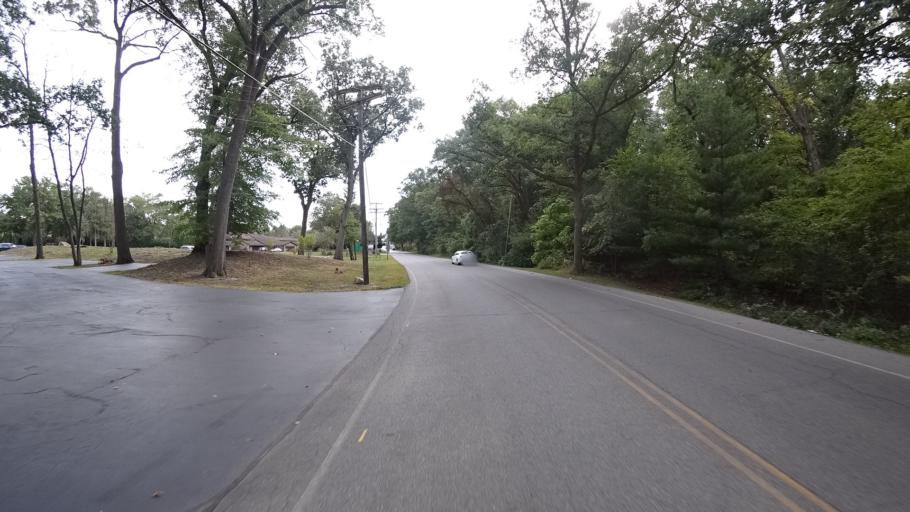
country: US
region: Indiana
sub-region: LaPorte County
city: Long Beach
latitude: 41.7392
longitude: -86.8557
